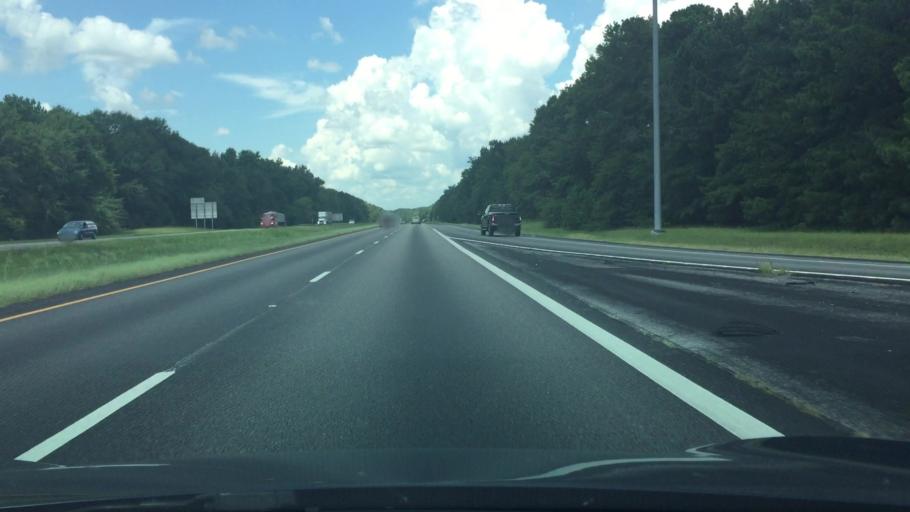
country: US
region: Alabama
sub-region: Macon County
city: Tuskegee
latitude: 32.4450
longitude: -85.7978
